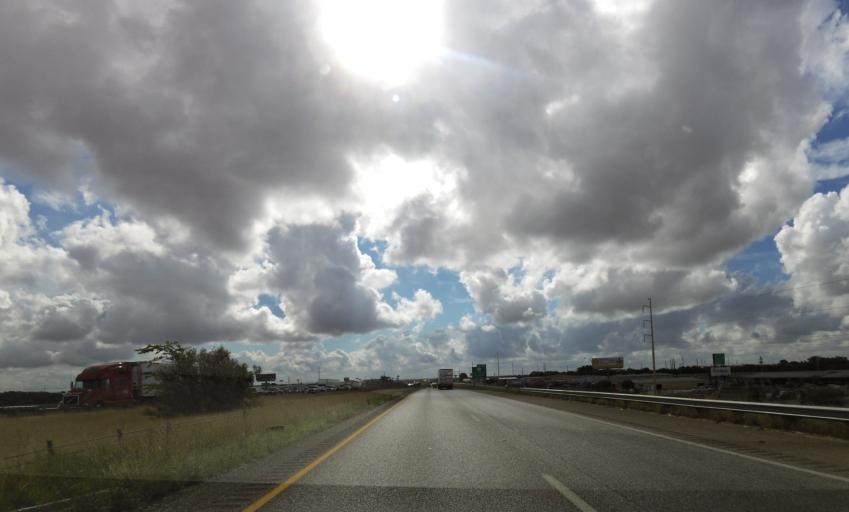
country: US
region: Texas
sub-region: Guadalupe County
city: Seguin
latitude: 29.5993
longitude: -97.9649
